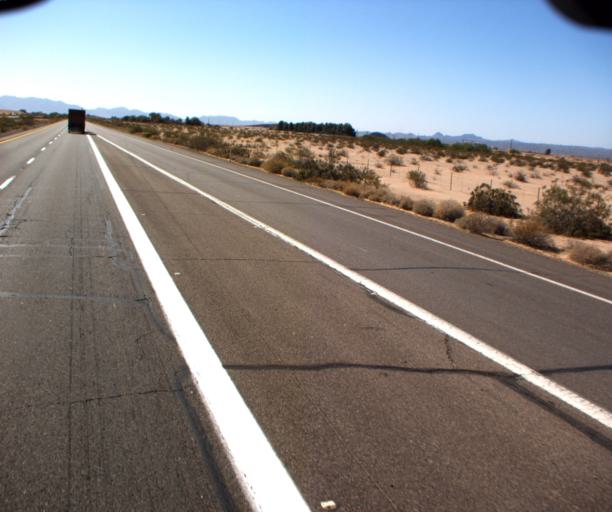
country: US
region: Arizona
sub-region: Yuma County
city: Wellton
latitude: 32.6810
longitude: -114.0256
